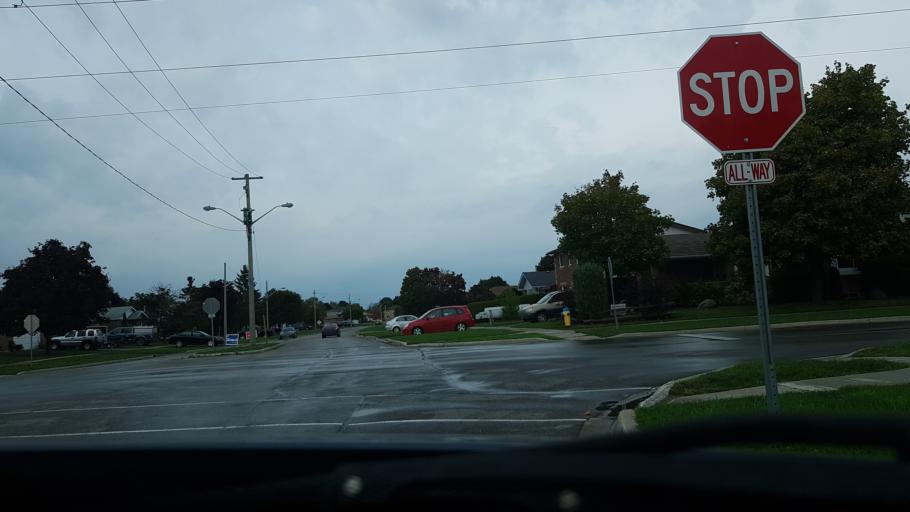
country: CA
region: Ontario
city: Omemee
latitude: 44.3690
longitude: -78.7477
